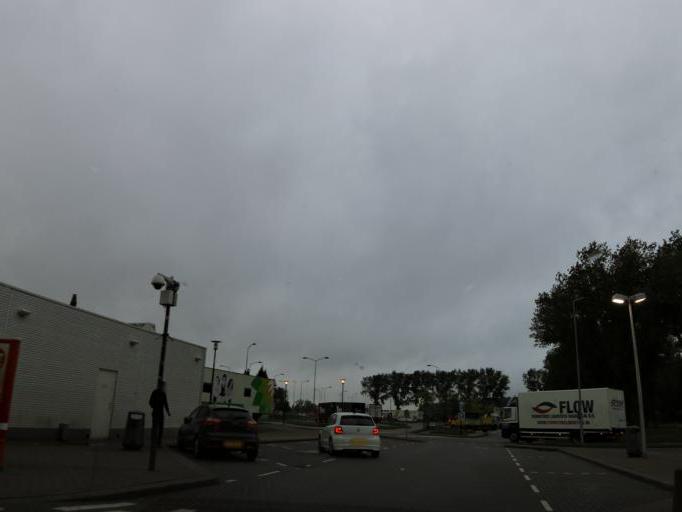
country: NL
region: Gelderland
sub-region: Gemeente Culemborg
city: Culemborg
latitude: 51.9120
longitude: 5.1810
